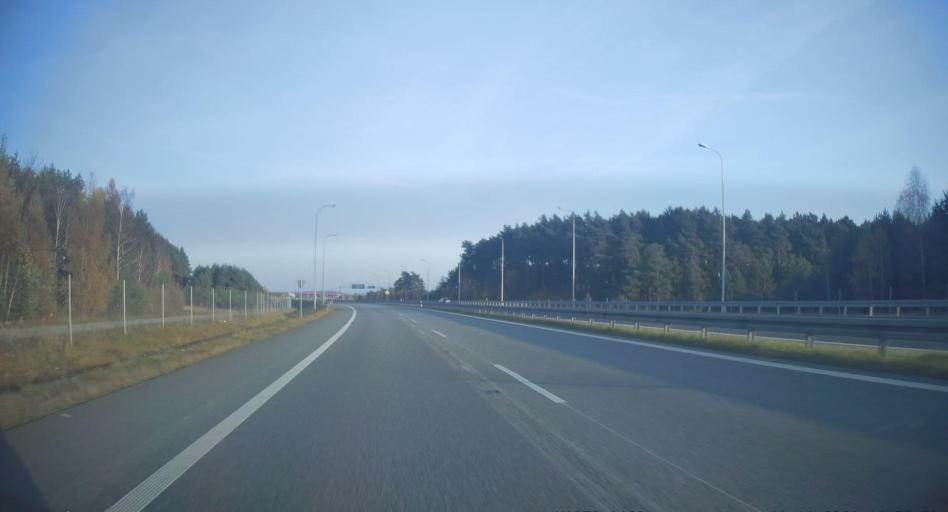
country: PL
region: Silesian Voivodeship
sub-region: Powiat bedzinski
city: Mierzecice
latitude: 50.4500
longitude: 19.1193
